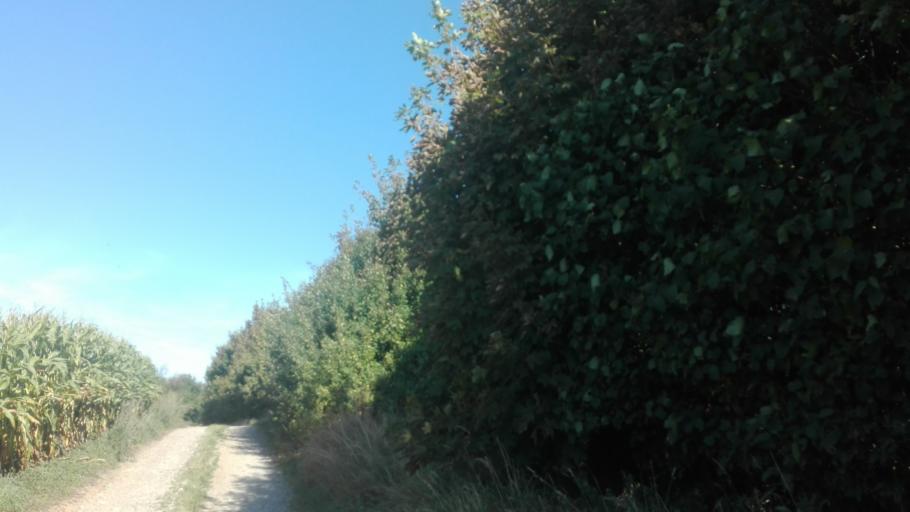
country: DK
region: Central Jutland
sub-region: Syddjurs Kommune
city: Ebeltoft
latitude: 56.2321
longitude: 10.7443
